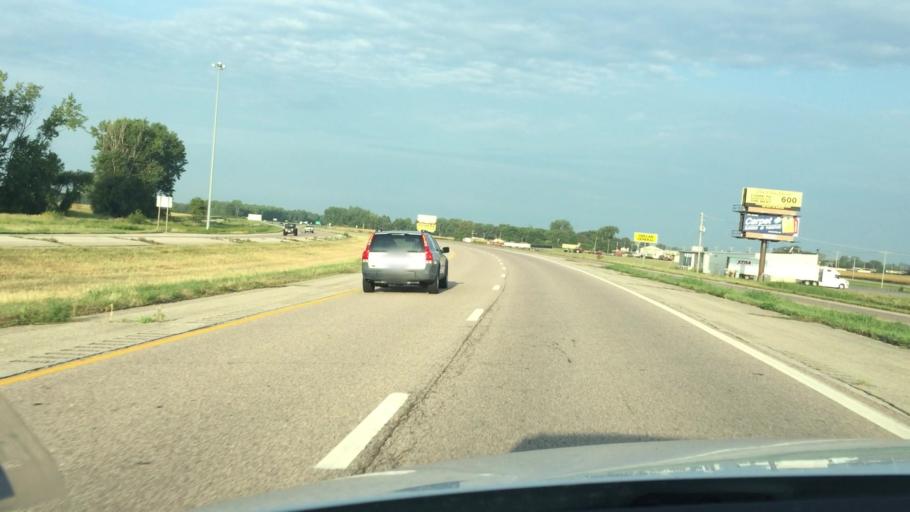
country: US
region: Kansas
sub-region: Doniphan County
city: Elwood
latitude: 39.7497
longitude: -94.8705
